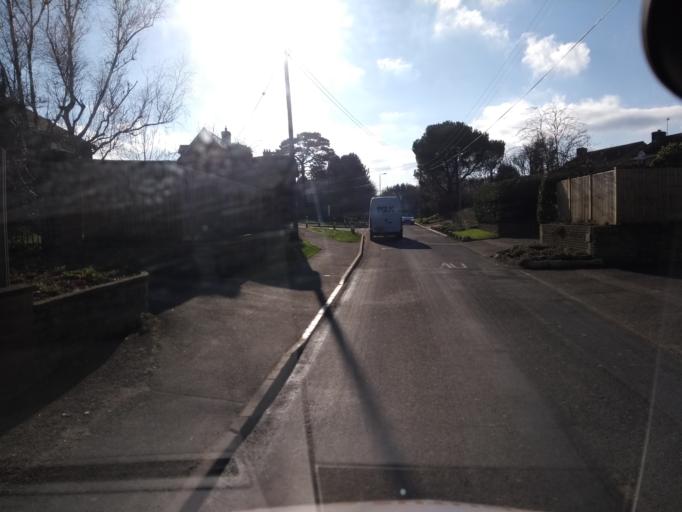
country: GB
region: England
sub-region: Somerset
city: South Petherton
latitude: 50.9441
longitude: -2.8031
